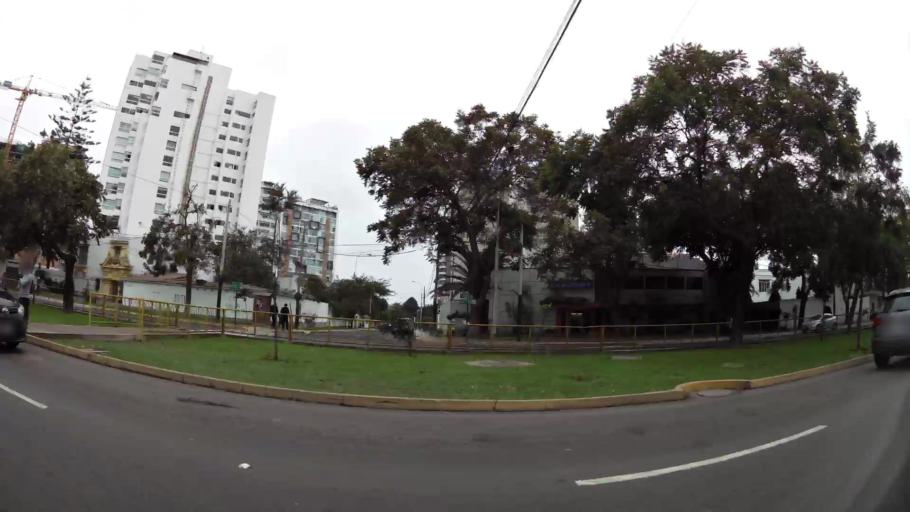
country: PE
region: Lima
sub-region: Lima
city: San Isidro
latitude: -12.0938
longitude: -77.0521
